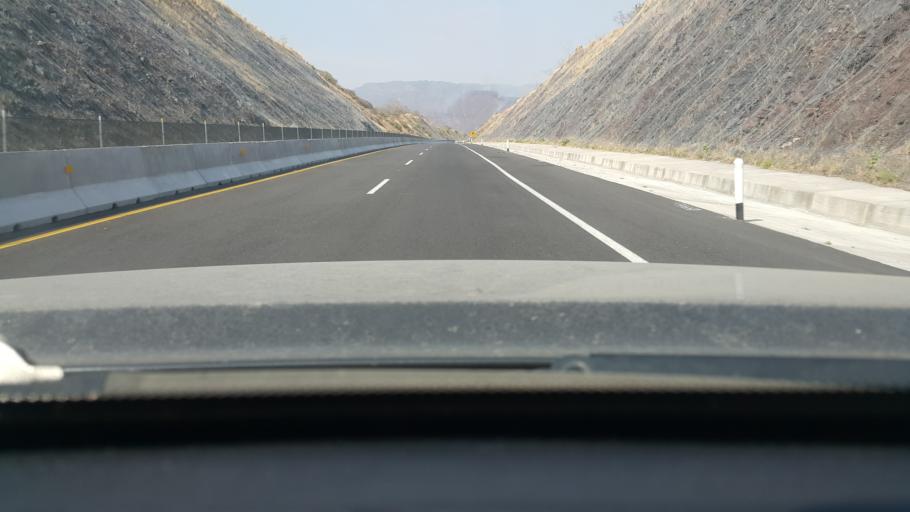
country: MX
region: Nayarit
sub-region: Ahuacatlan
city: Ahuacatlan
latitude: 21.0702
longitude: -104.4587
